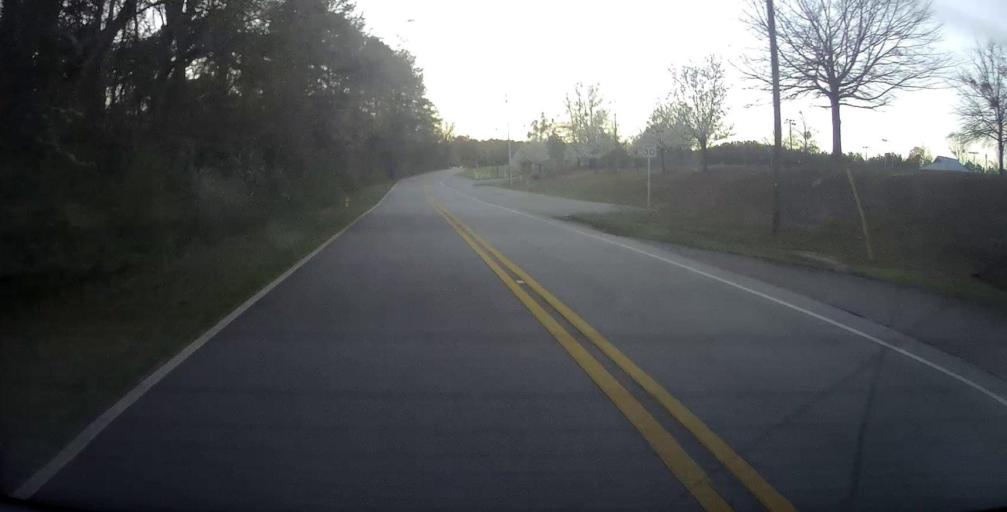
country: US
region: Alabama
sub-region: Russell County
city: Phenix City
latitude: 32.4996
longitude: -85.0039
